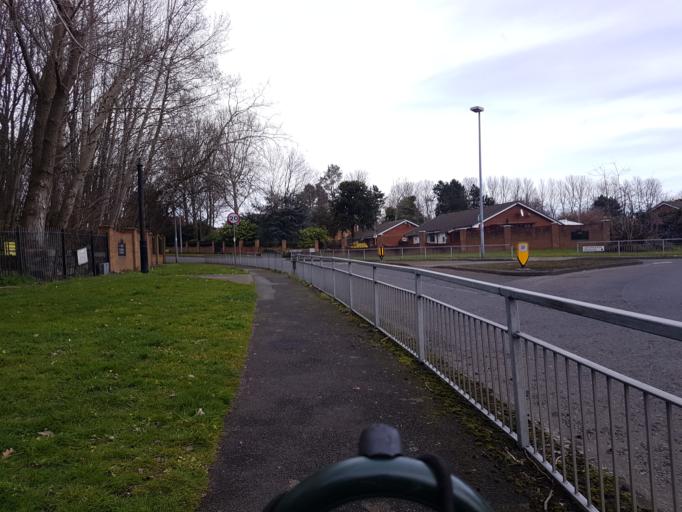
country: GB
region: England
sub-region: Metropolitan Borough of Wirral
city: Bromborough
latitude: 53.3749
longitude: -2.9598
